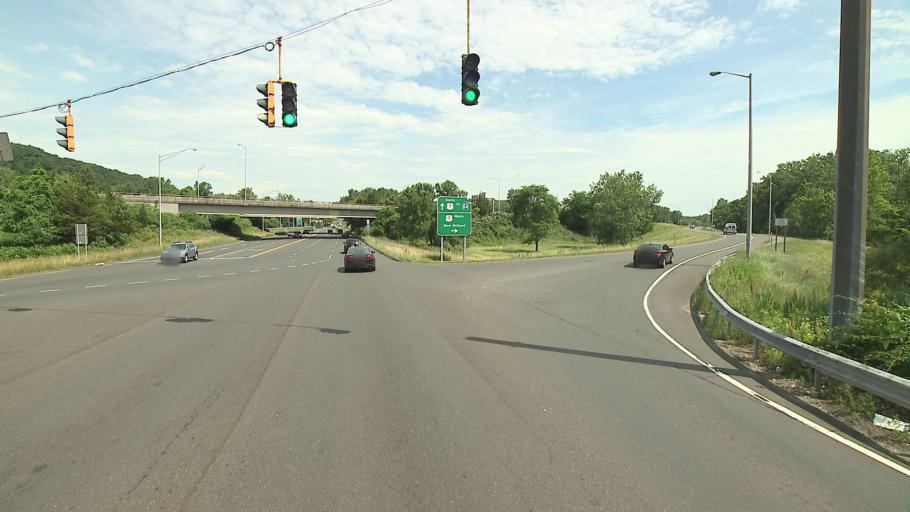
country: US
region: Connecticut
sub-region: Fairfield County
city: Danbury
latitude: 41.4299
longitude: -73.4101
